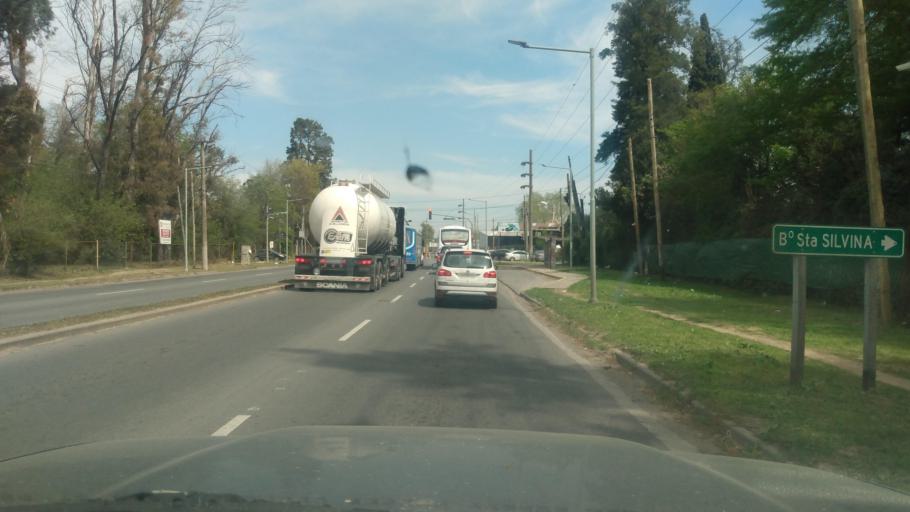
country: AR
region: Buenos Aires
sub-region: Partido de Pilar
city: Pilar
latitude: -34.4414
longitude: -58.8988
